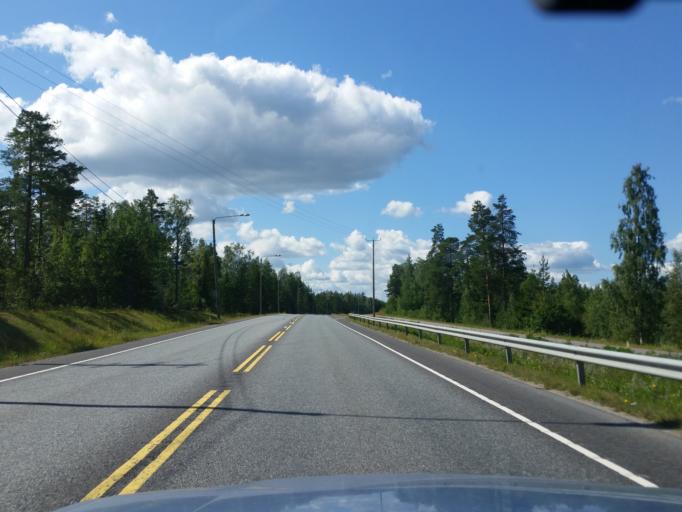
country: FI
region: Uusimaa
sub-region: Helsinki
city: Vihti
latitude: 60.3186
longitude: 24.2603
